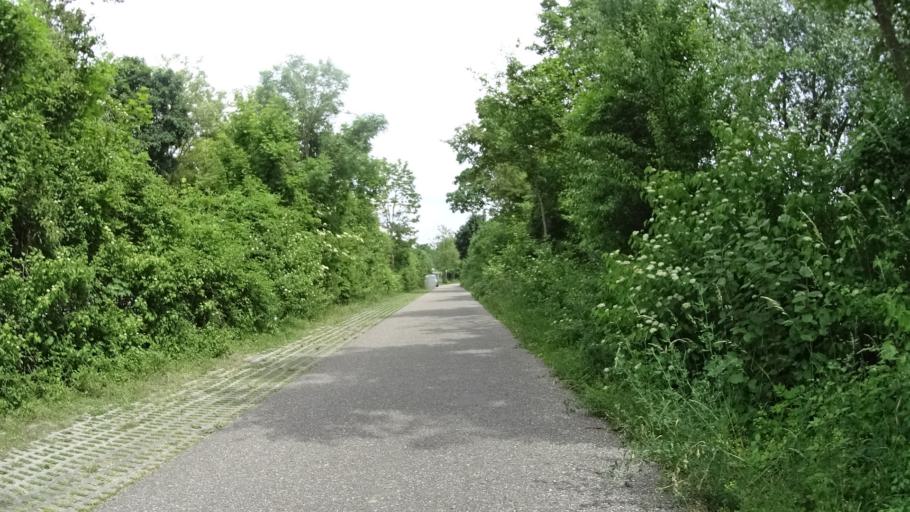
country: DE
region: Bavaria
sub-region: Upper Palatinate
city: Donaustauf
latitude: 49.0293
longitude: 12.2212
